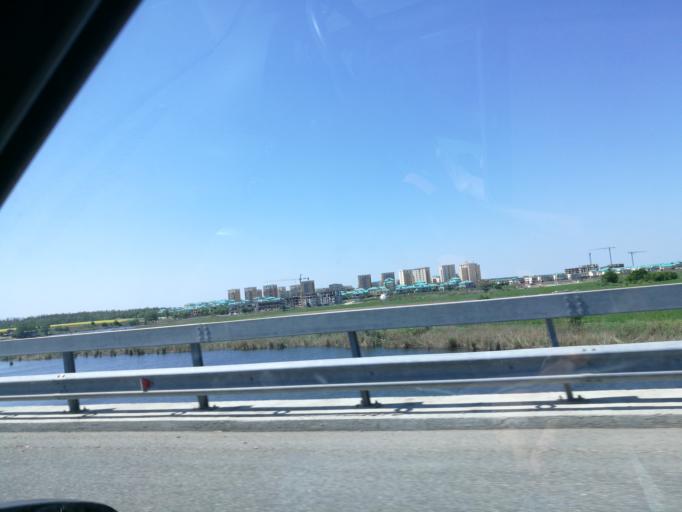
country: RO
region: Ilfov
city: Stefanestii de Jos
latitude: 44.5355
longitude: 26.1835
